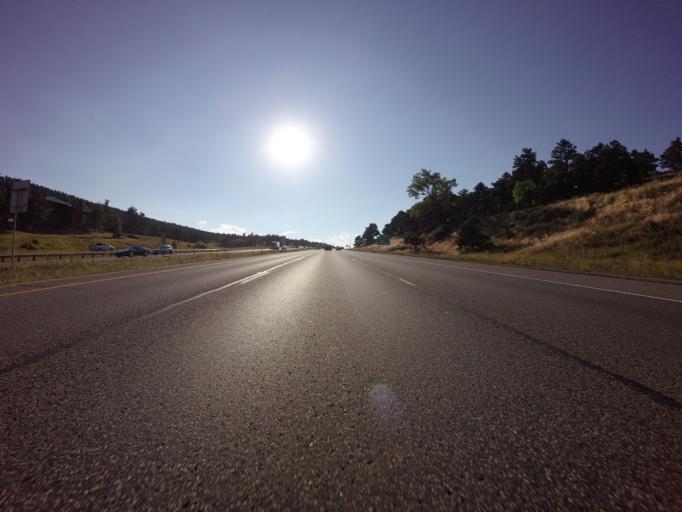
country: US
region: Colorado
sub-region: Jefferson County
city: Genesee
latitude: 39.7093
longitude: -105.2877
